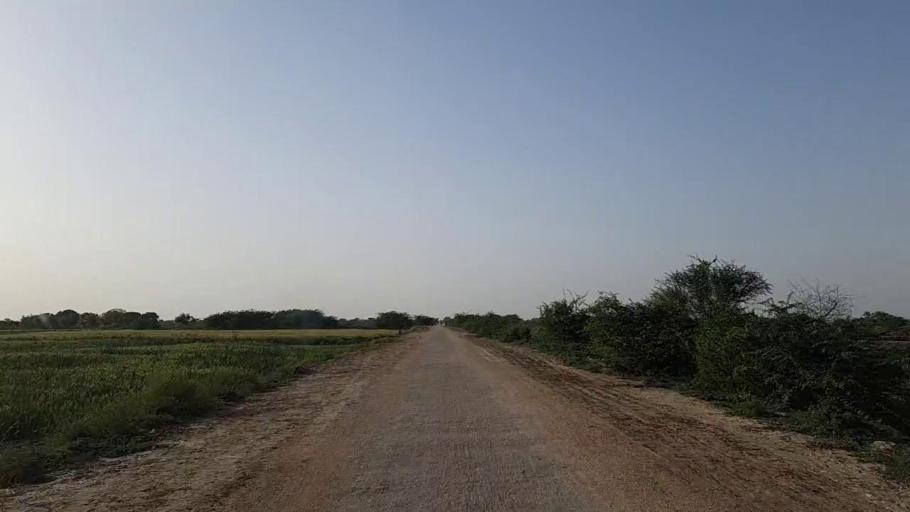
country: PK
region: Sindh
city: Jati
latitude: 24.3303
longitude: 68.1591
